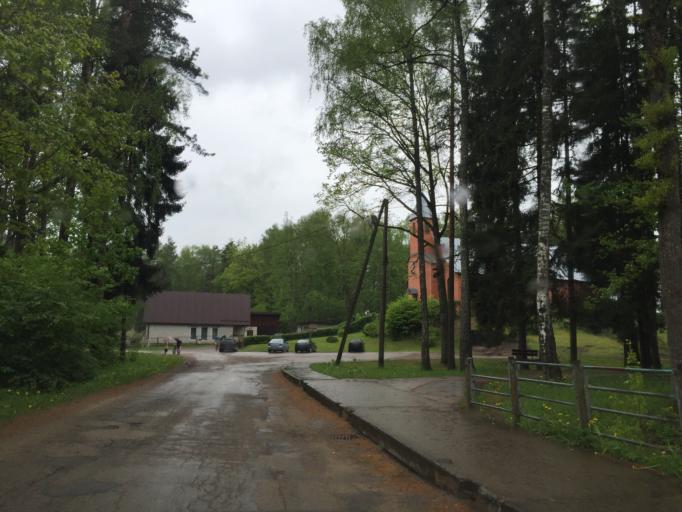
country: LV
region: Lielvarde
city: Lielvarde
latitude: 56.7299
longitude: 24.8052
